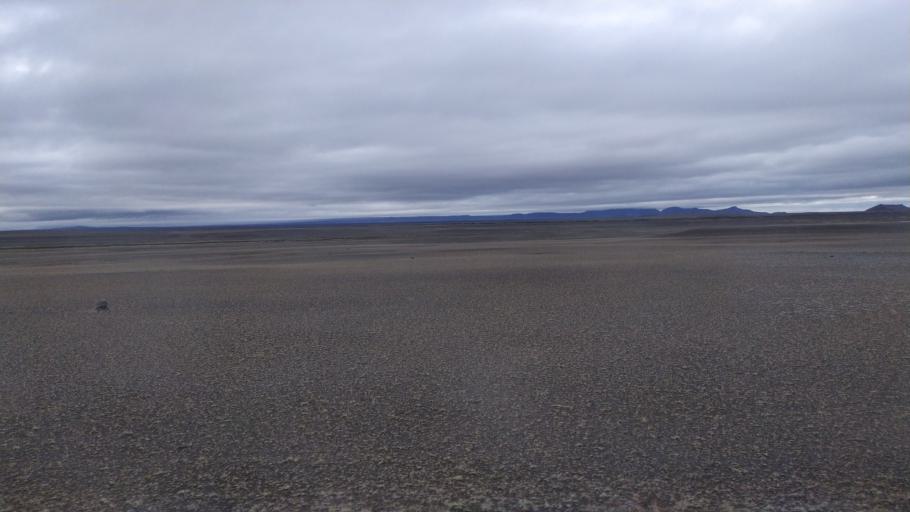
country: IS
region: Northeast
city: Laugar
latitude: 65.6121
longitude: -16.1578
